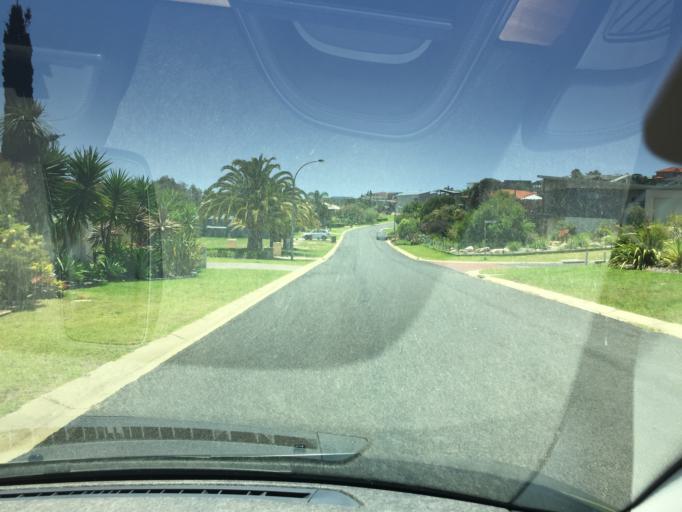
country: AU
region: New South Wales
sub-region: Bega Valley
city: Merimbula
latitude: -36.8493
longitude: 149.9316
